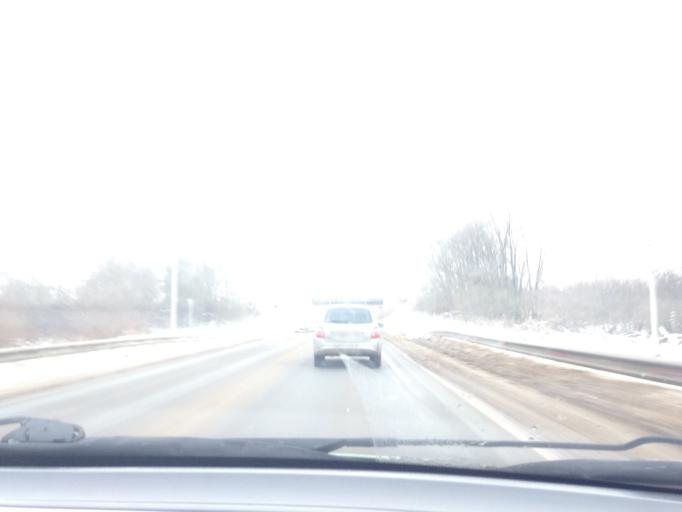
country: RU
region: Tula
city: Pervomayskiy
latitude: 54.0315
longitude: 37.5227
